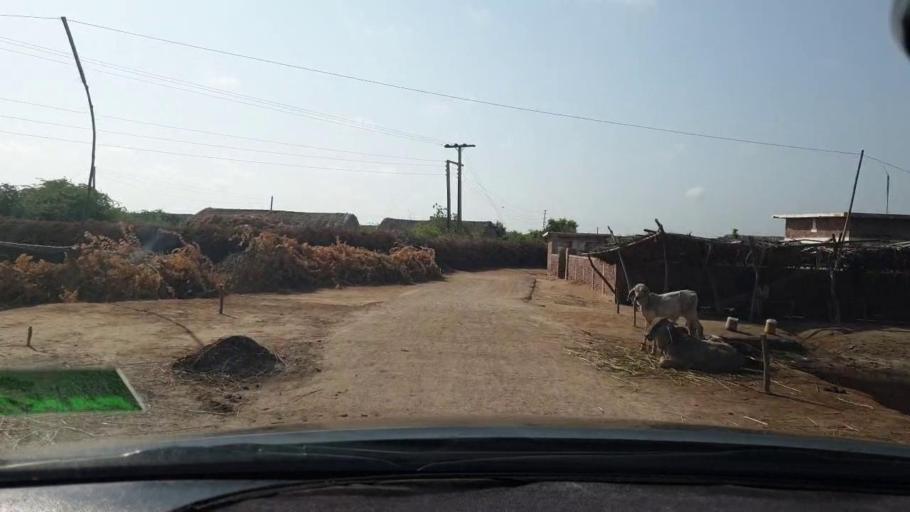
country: PK
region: Sindh
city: Tando Bago
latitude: 24.8614
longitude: 68.9927
